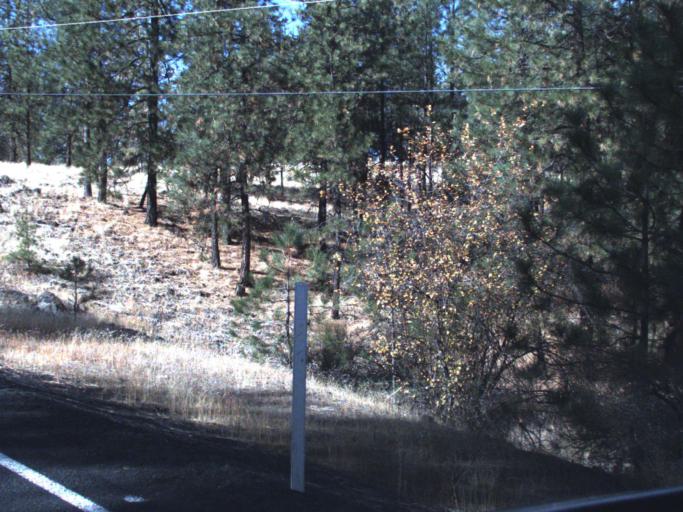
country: US
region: Washington
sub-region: Lincoln County
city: Davenport
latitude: 47.8232
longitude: -118.1860
